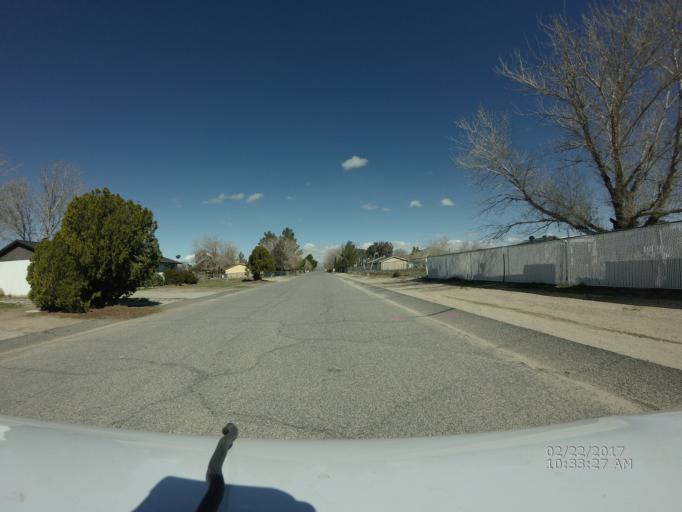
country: US
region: California
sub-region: Los Angeles County
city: Lake Los Angeles
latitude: 34.6251
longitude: -117.8236
